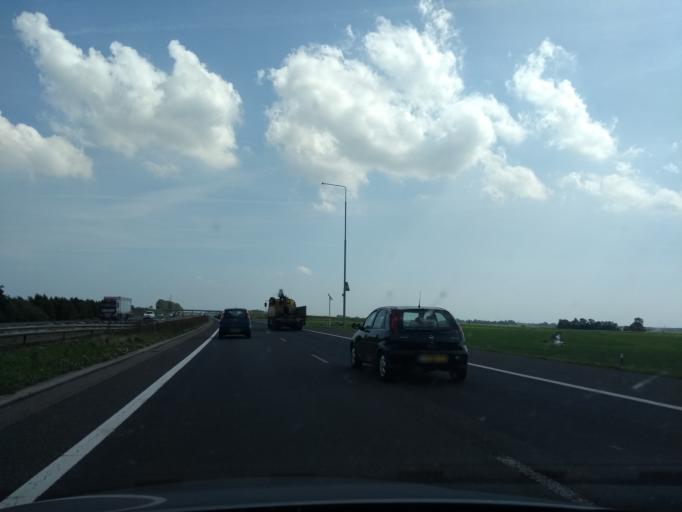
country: NL
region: Friesland
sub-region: Gemeente Skarsterlan
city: Joure
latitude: 52.9654
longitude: 5.7668
